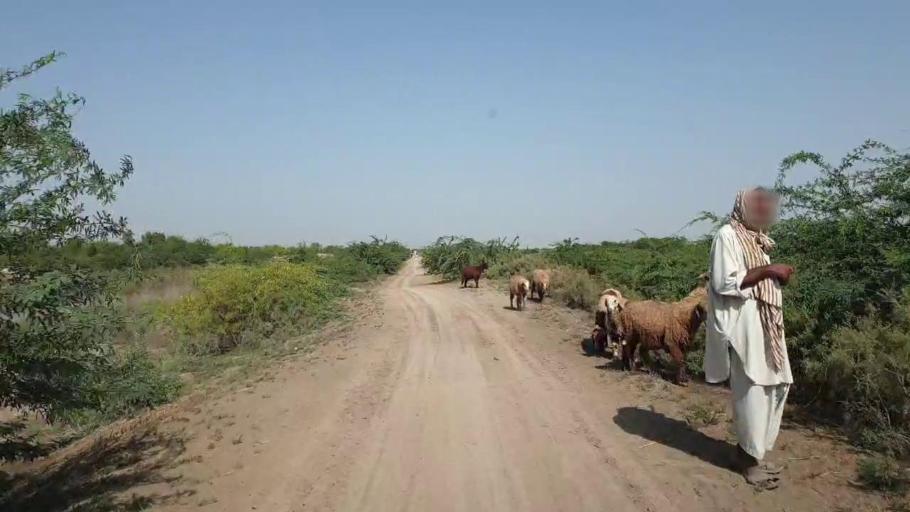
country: PK
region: Sindh
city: Tando Bago
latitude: 24.6580
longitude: 69.0698
